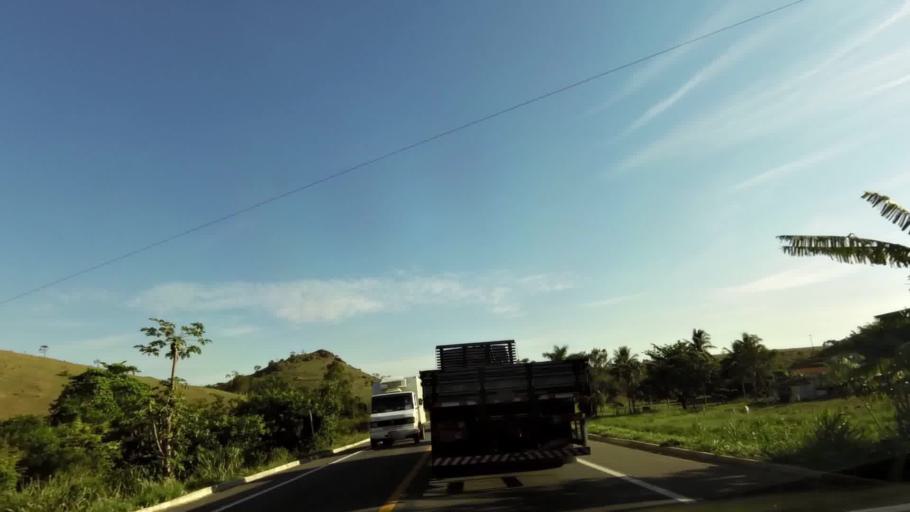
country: BR
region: Espirito Santo
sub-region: Viana
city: Viana
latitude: -20.5001
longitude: -40.4755
